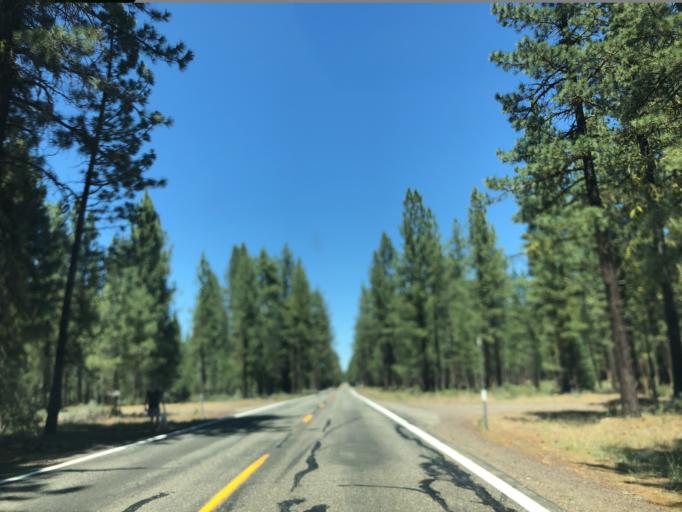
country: US
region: California
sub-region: Shasta County
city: Burney
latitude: 40.6537
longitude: -121.4581
